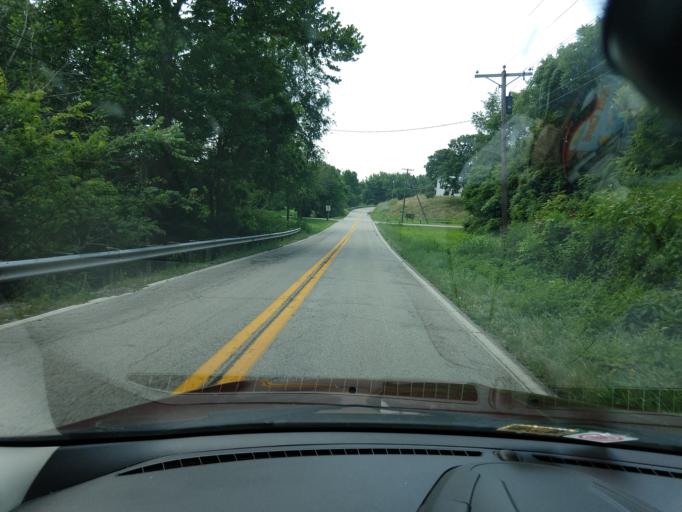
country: US
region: West Virginia
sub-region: Mason County
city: New Haven
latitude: 38.9270
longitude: -81.9133
